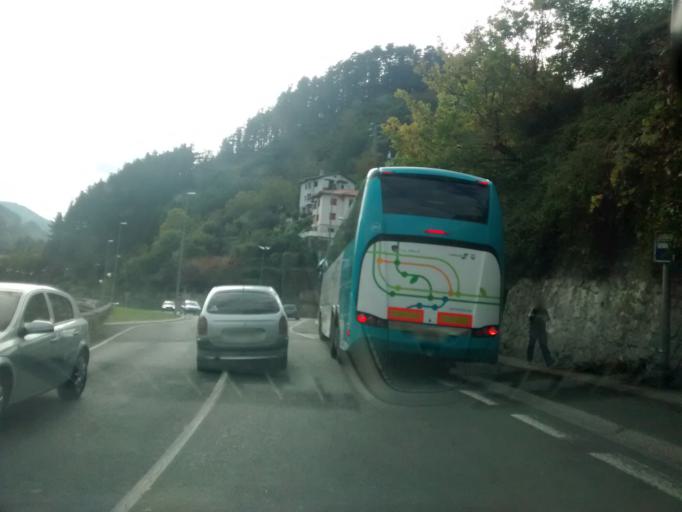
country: ES
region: Basque Country
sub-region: Provincia de Guipuzcoa
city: Elgoibar
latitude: 43.2158
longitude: -2.4168
